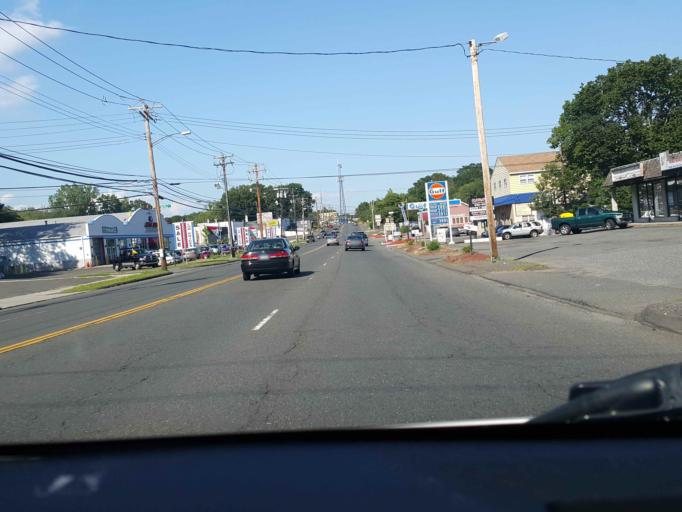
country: US
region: Connecticut
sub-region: New Haven County
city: West Haven
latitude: 41.2871
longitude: -72.9742
